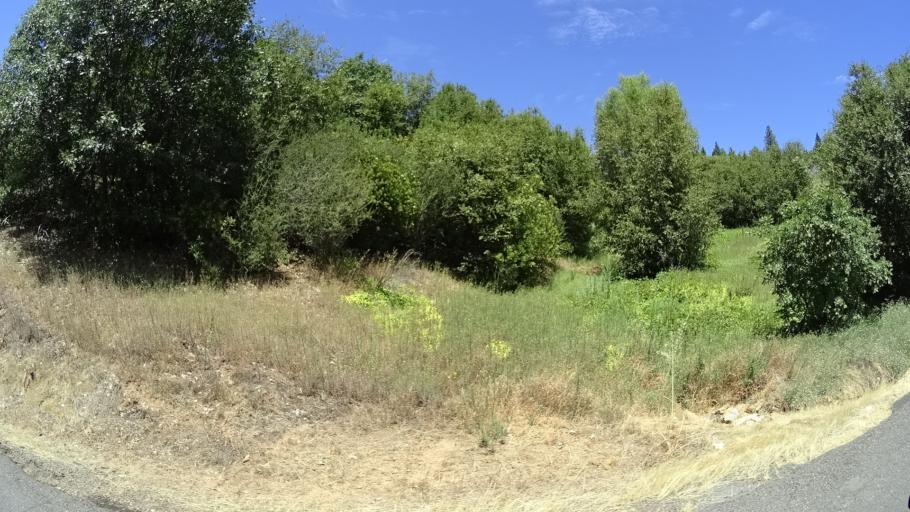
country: US
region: California
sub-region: Calaveras County
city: Forest Meadows
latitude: 38.1891
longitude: -120.4439
